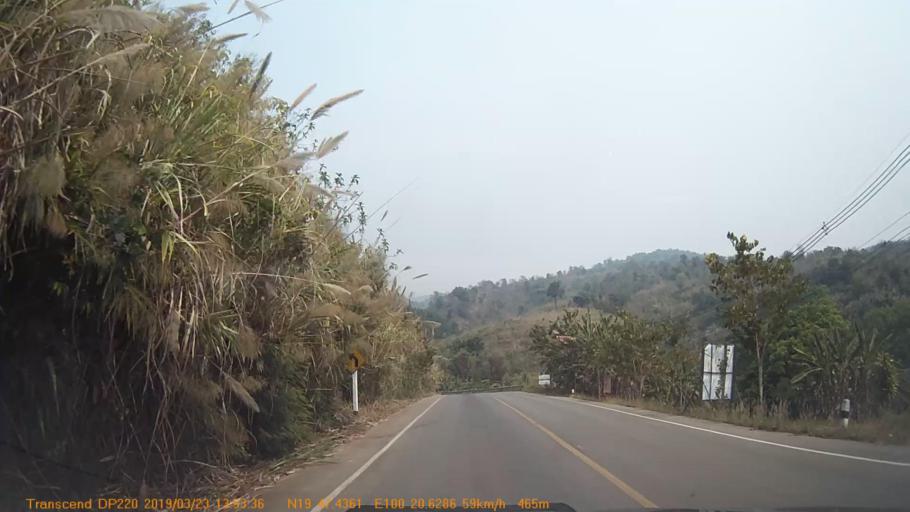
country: TH
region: Chiang Rai
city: Khun Tan
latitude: 19.7906
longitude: 100.3440
